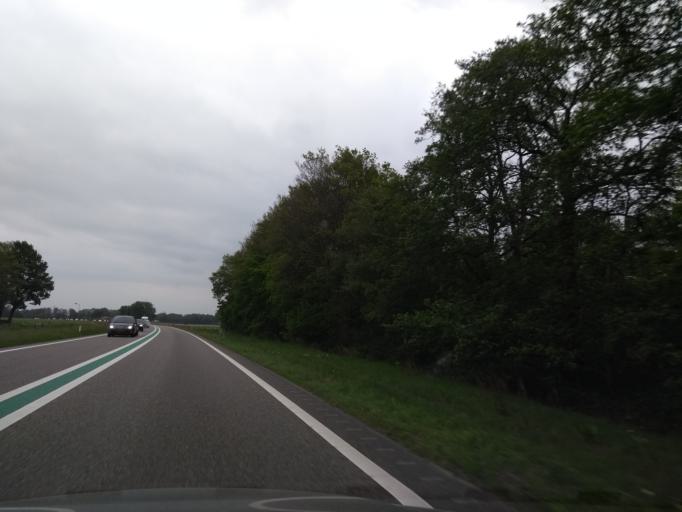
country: NL
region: Overijssel
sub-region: Gemeente Twenterand
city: Den Ham
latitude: 52.5787
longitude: 6.4154
